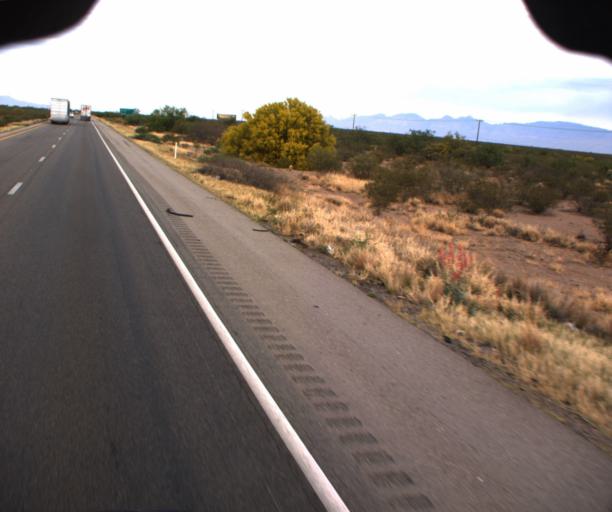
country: US
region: Arizona
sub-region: Pima County
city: Vail
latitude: 32.0361
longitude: -110.7311
